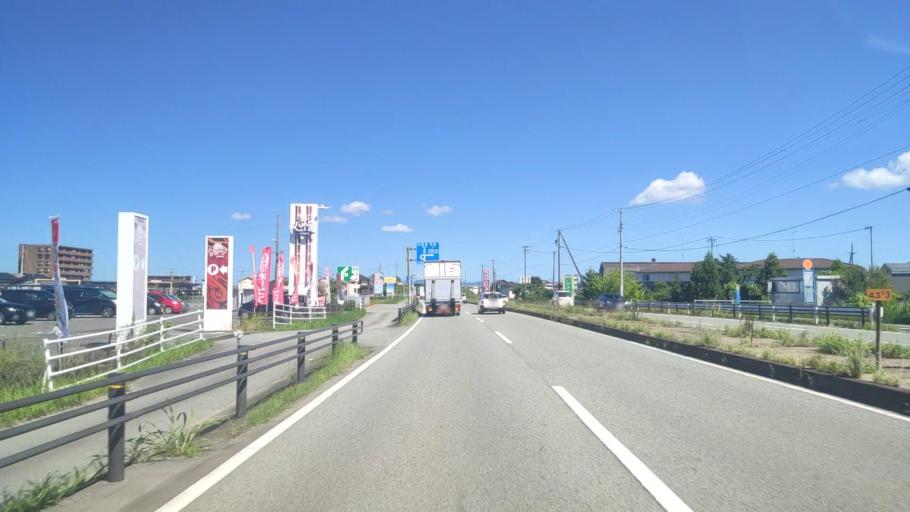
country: JP
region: Mie
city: Hisai-motomachi
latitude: 34.5883
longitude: 136.5491
